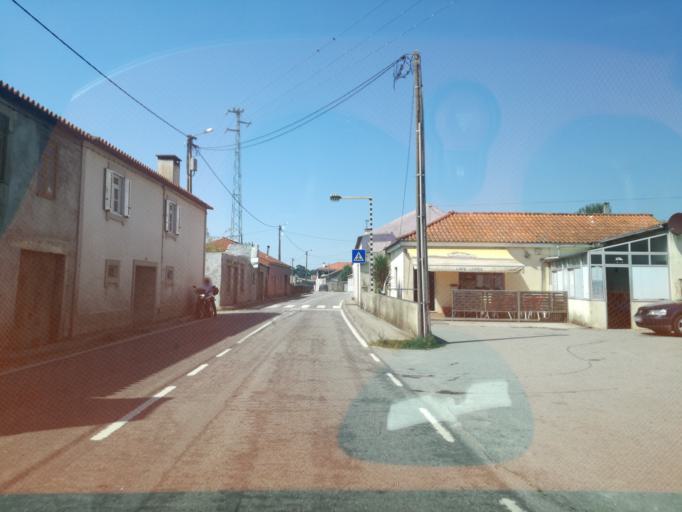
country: PT
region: Braga
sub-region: Esposende
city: Apulia
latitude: 41.4921
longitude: -8.7546
